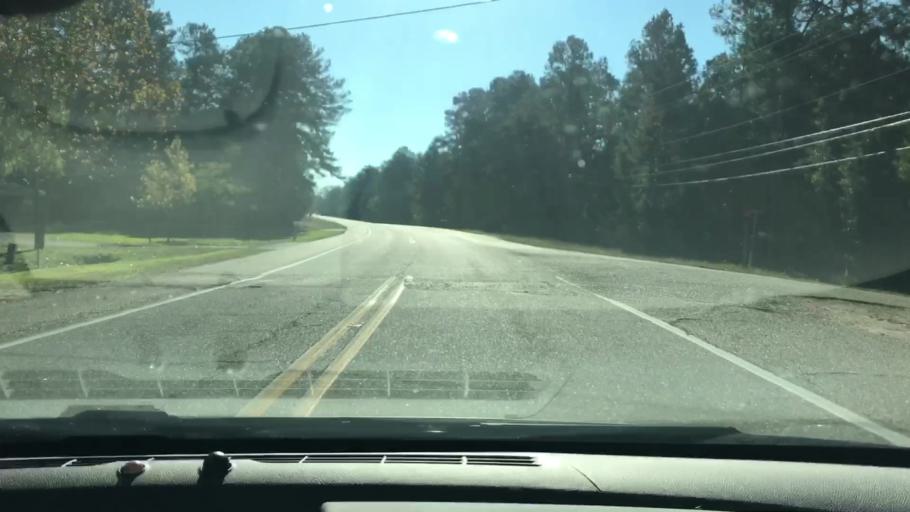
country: US
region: Louisiana
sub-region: Saint Tammany Parish
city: Pearl River
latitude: 30.4456
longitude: -89.7972
